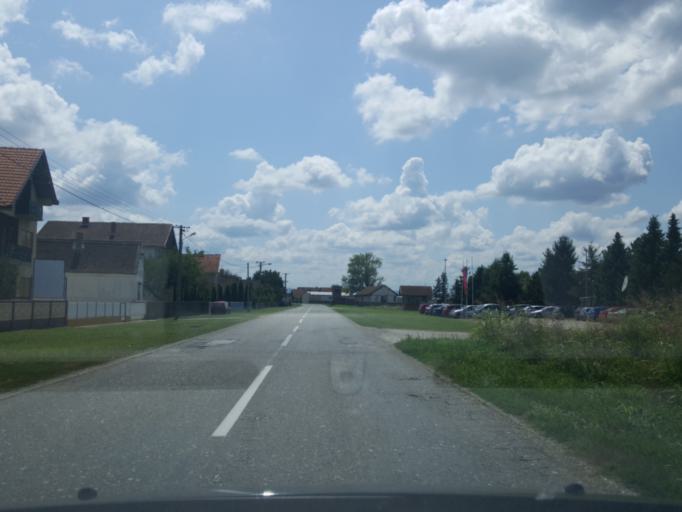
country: RS
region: Central Serbia
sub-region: Macvanski Okrug
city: Bogatic
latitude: 44.8230
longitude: 19.4776
